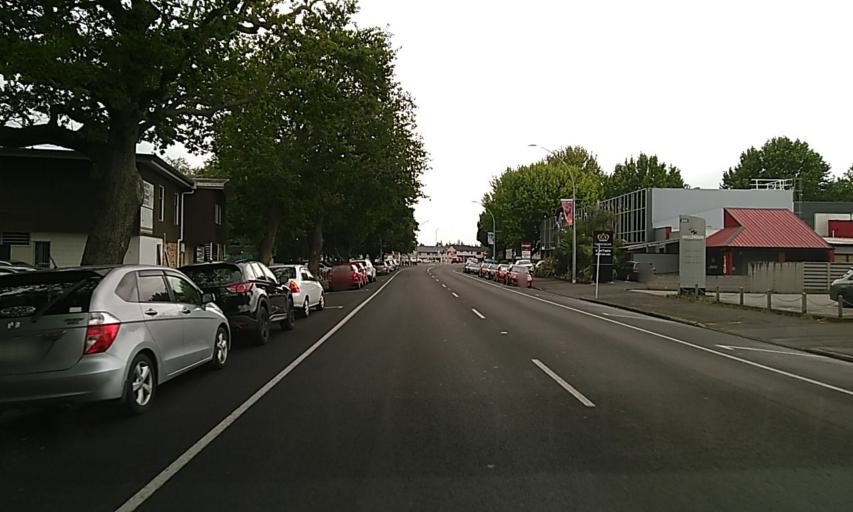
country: NZ
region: Waikato
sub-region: Hamilton City
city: Hamilton
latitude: -37.7831
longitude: 175.2723
